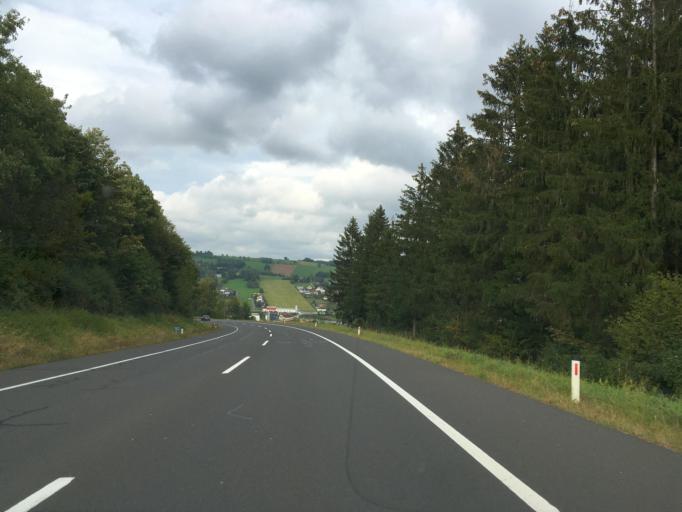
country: AT
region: Styria
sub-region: Politischer Bezirk Hartberg-Fuerstenfeld
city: Pinggau
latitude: 47.4309
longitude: 16.0633
